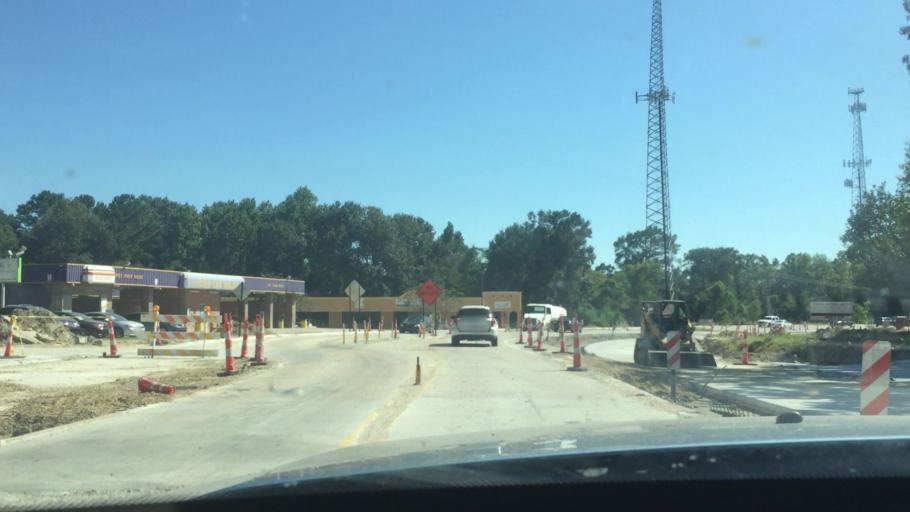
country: US
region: Louisiana
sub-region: East Baton Rouge Parish
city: Shenandoah
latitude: 30.4206
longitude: -91.0075
